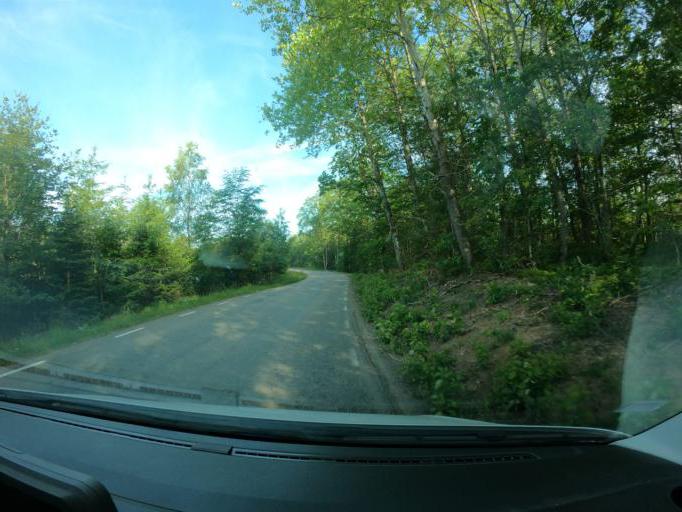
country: SE
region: Skane
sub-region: Angelholms Kommun
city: Munka-Ljungby
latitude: 56.3212
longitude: 12.9754
